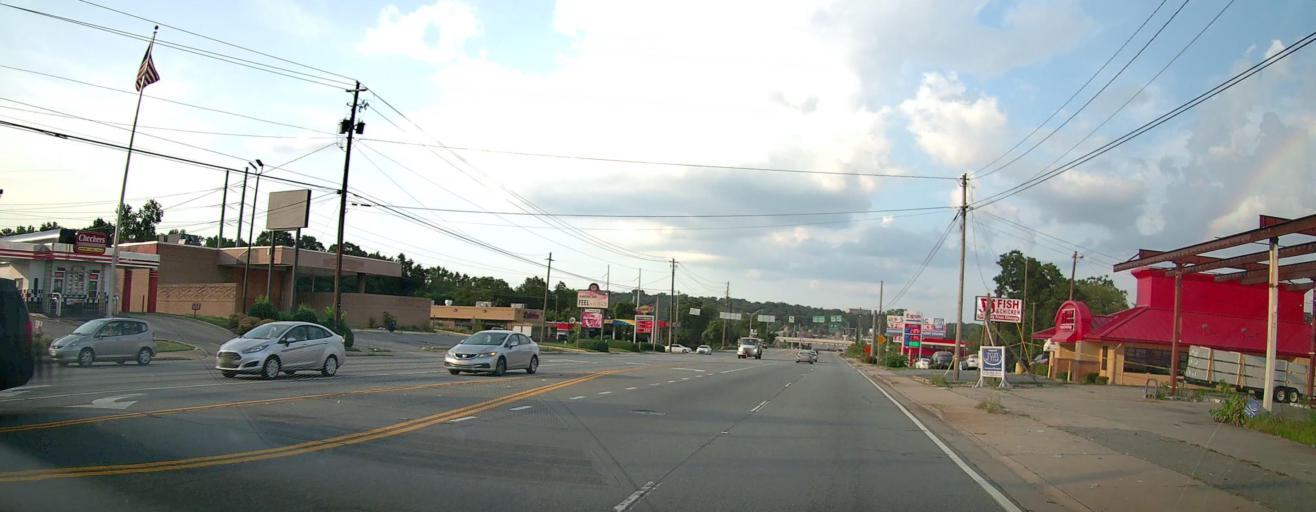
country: US
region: Georgia
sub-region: Bibb County
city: Macon
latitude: 32.8438
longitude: -83.6307
